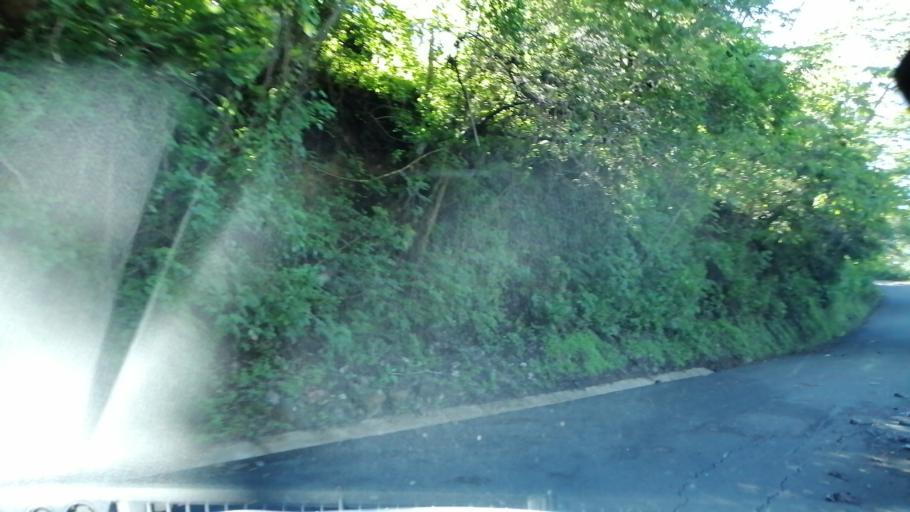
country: SV
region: Morazan
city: Corinto
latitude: 13.7909
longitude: -88.0135
